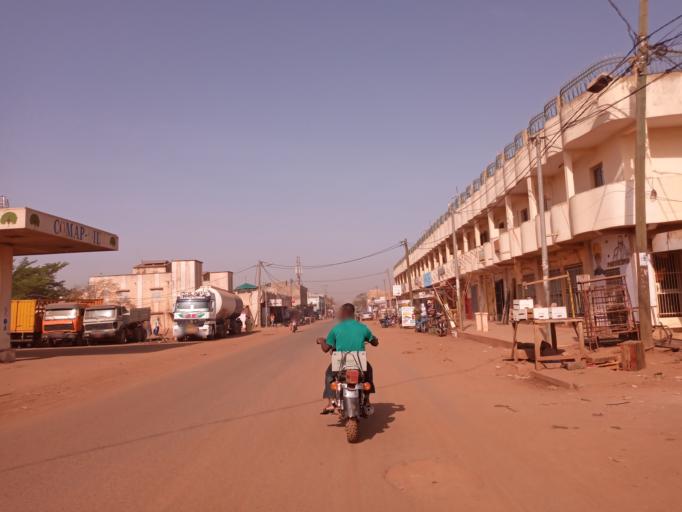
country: ML
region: Bamako
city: Bamako
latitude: 12.5884
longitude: -7.9677
